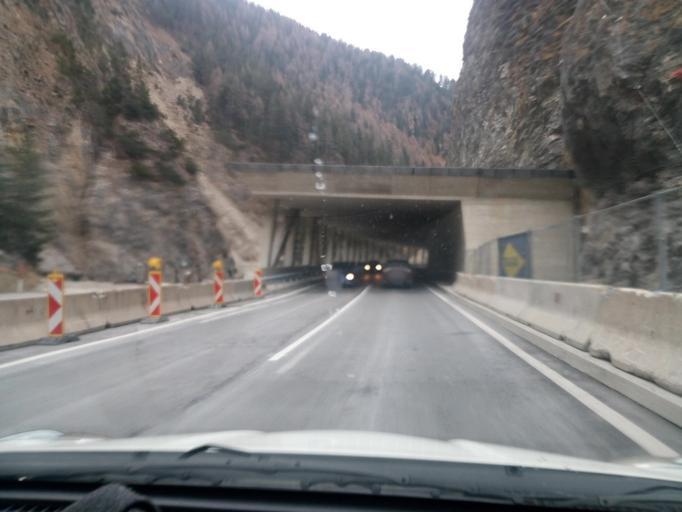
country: AT
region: Tyrol
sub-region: Politischer Bezirk Landeck
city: Nauders
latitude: 46.9131
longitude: 10.4933
